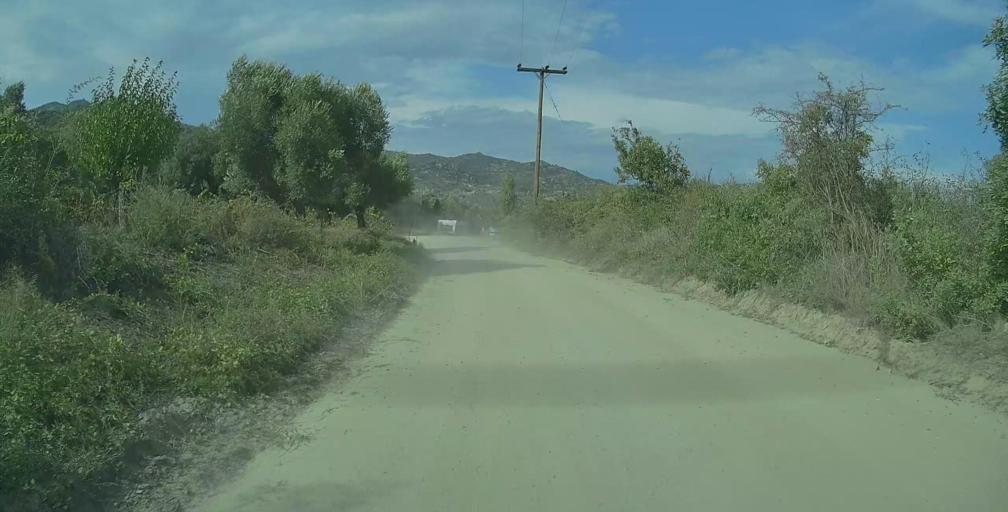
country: GR
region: Central Macedonia
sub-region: Nomos Chalkidikis
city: Sykia
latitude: 40.0290
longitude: 23.9445
